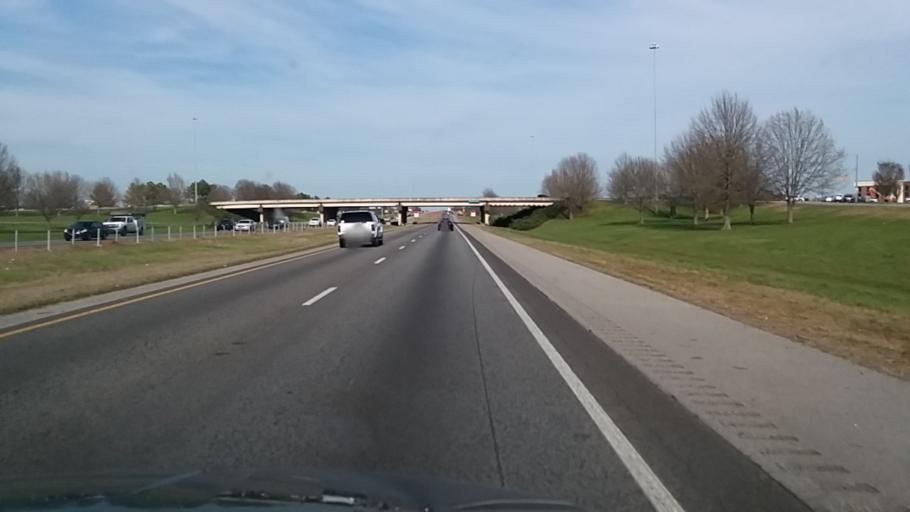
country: US
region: Alabama
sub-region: Madison County
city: Madison
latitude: 34.6724
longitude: -86.7546
